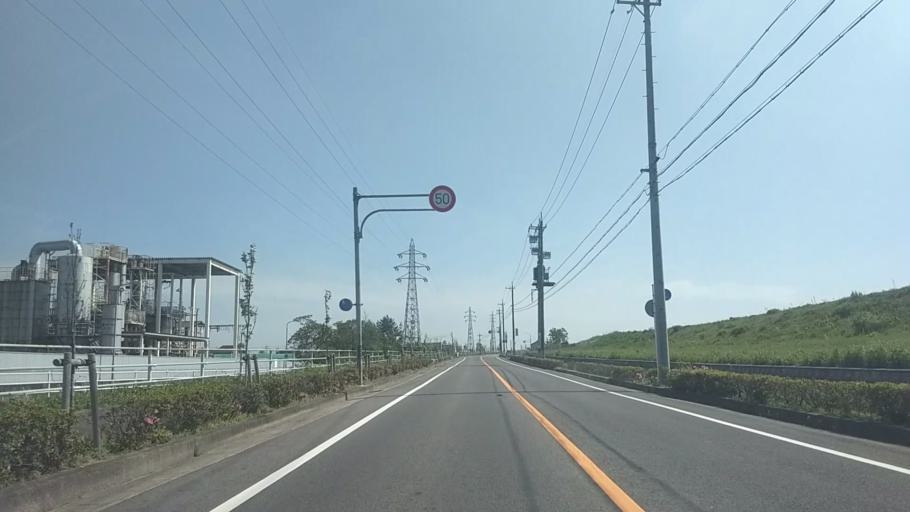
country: JP
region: Aichi
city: Okazaki
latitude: 34.9784
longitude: 137.1503
